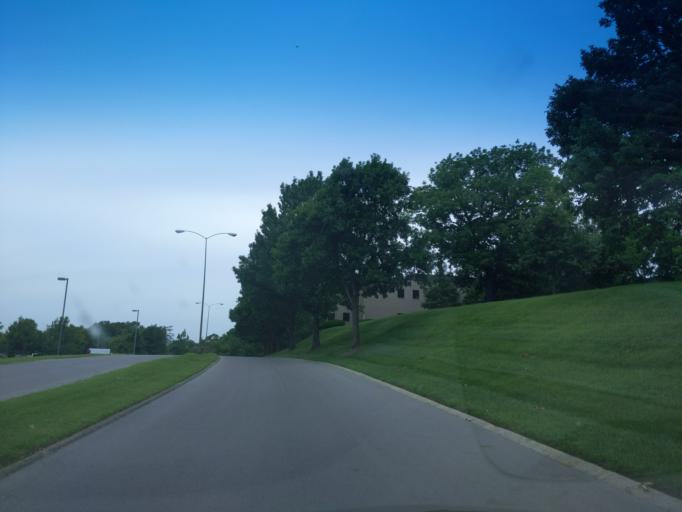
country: US
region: Tennessee
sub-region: Williamson County
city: Brentwood
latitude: 36.0315
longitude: -86.7795
